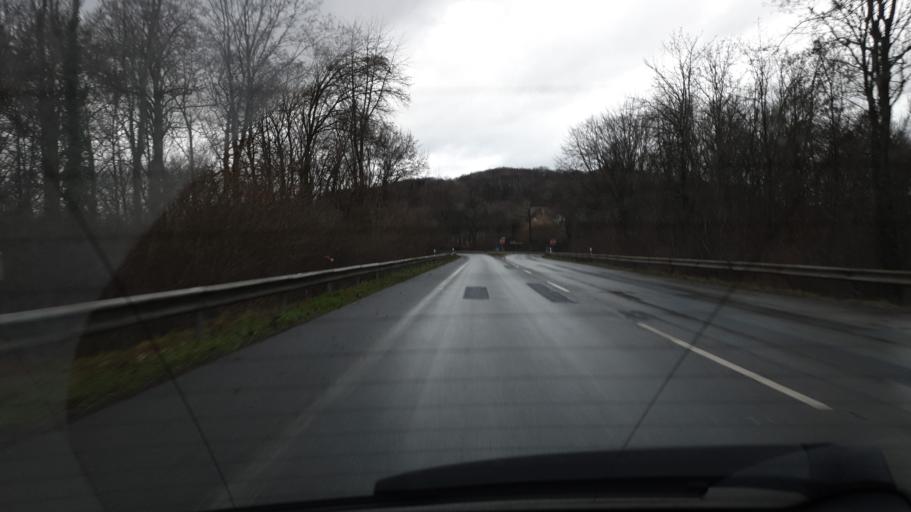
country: DE
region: North Rhine-Westphalia
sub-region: Regierungsbezirk Detmold
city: Vlotho
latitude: 52.1405
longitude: 8.8303
